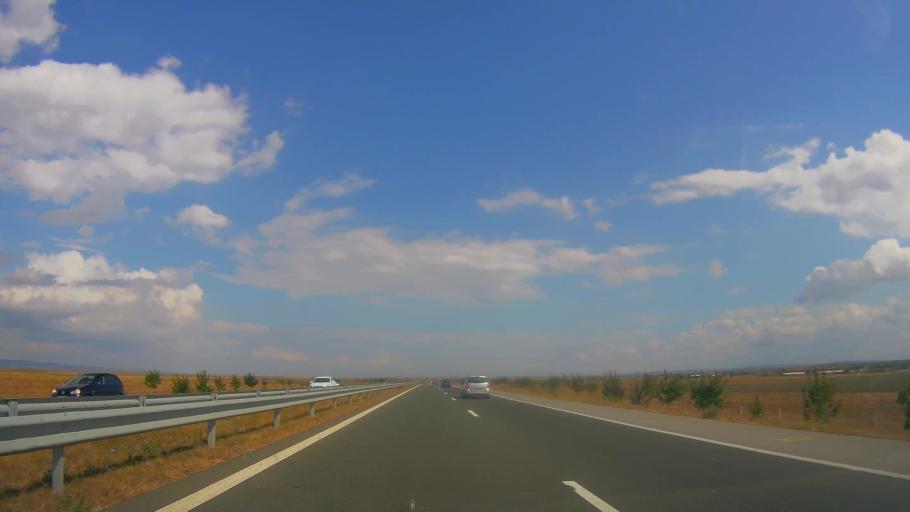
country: BG
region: Yambol
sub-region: Obshtina Straldzha
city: Straldzha
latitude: 42.5581
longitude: 26.6079
